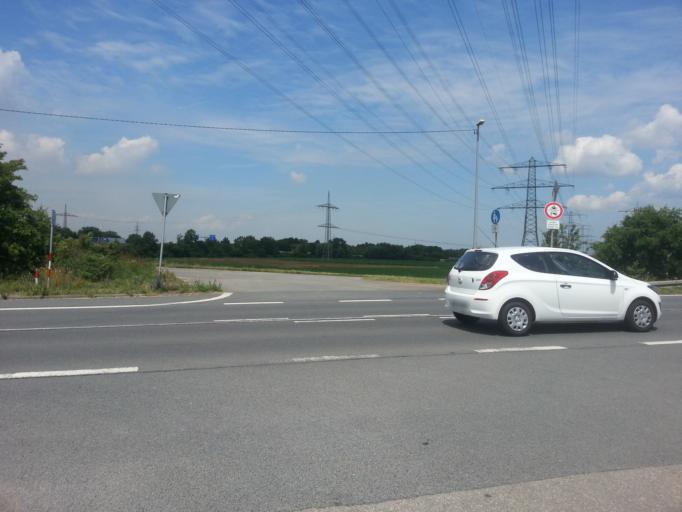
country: DE
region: Baden-Wuerttemberg
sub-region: Karlsruhe Region
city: Ilvesheim
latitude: 49.4559
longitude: 8.5439
